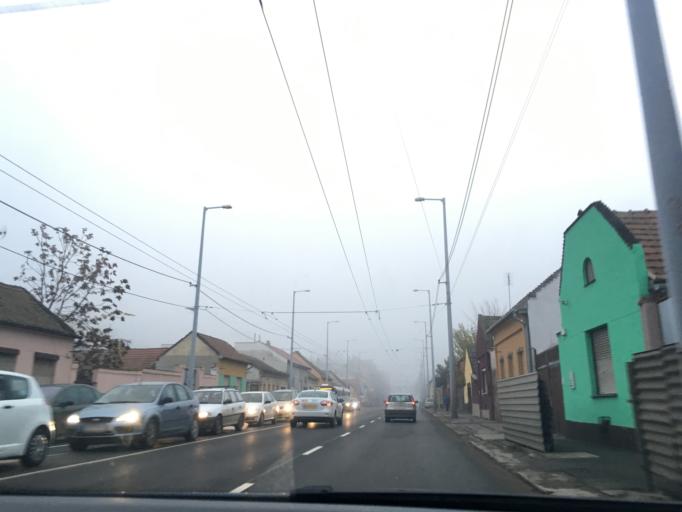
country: HU
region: Hajdu-Bihar
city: Debrecen
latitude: 47.5358
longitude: 21.6388
